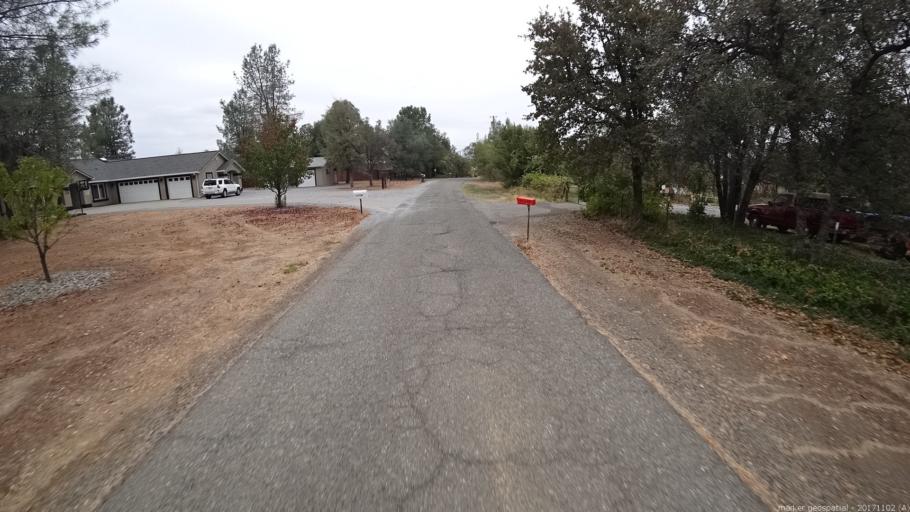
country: US
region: California
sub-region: Shasta County
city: Bella Vista
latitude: 40.6288
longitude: -122.2929
